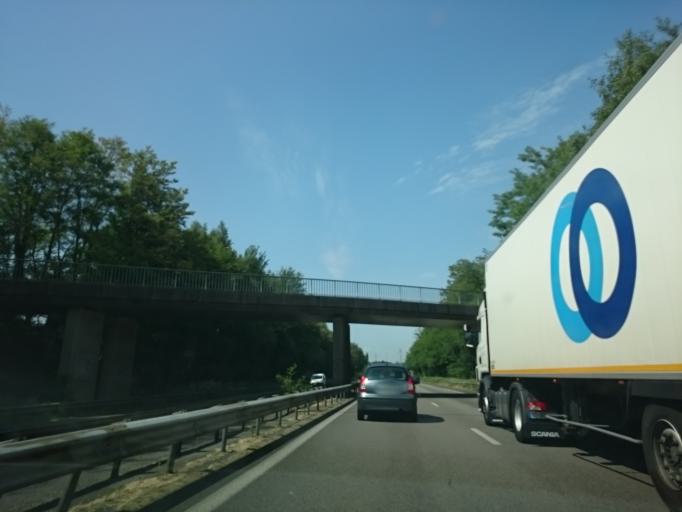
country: FR
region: Pays de la Loire
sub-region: Departement de la Loire-Atlantique
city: Treillieres
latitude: 47.3539
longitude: -1.6561
